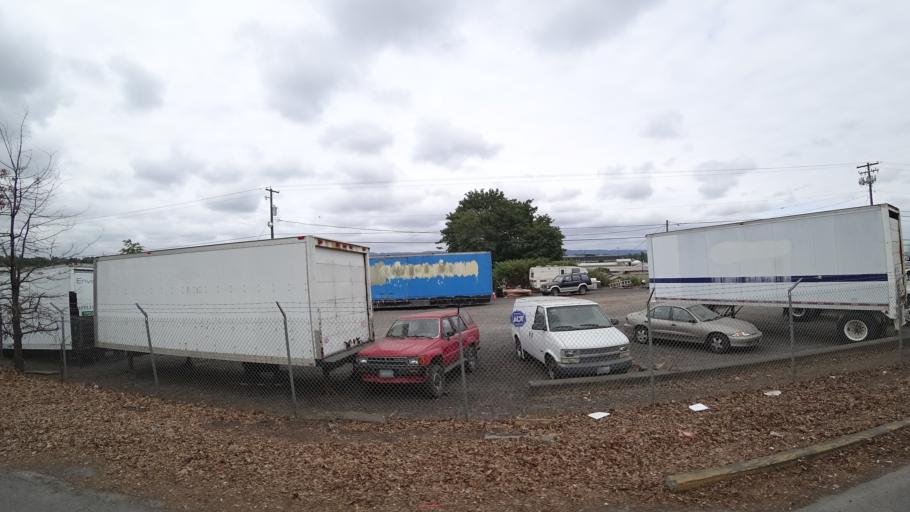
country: US
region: Washington
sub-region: Clark County
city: Vancouver
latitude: 45.5903
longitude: -122.6665
